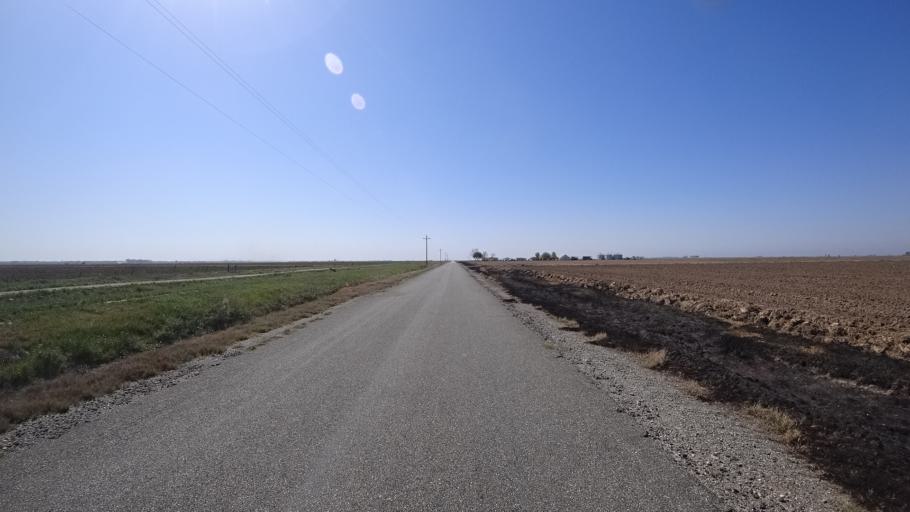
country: US
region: California
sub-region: Glenn County
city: Willows
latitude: 39.5122
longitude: -122.0654
